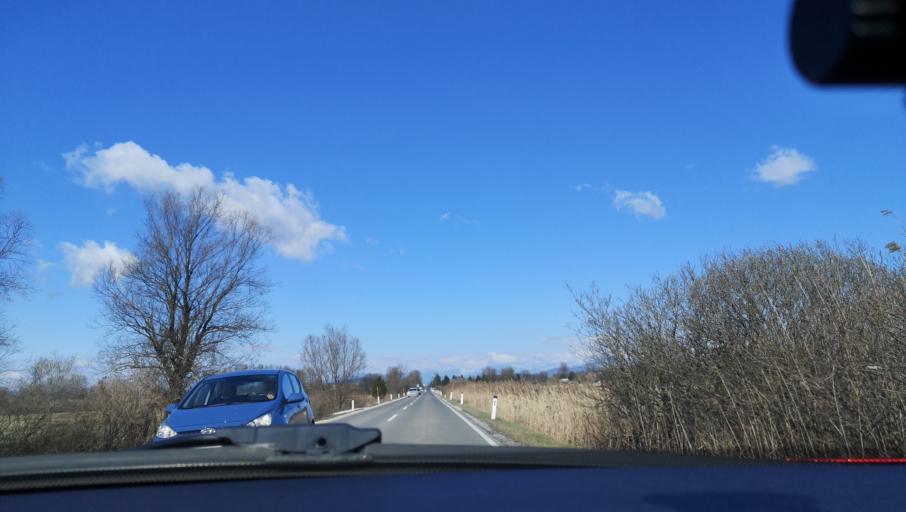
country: SI
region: Ig
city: Ig
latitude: 45.9931
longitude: 14.5189
